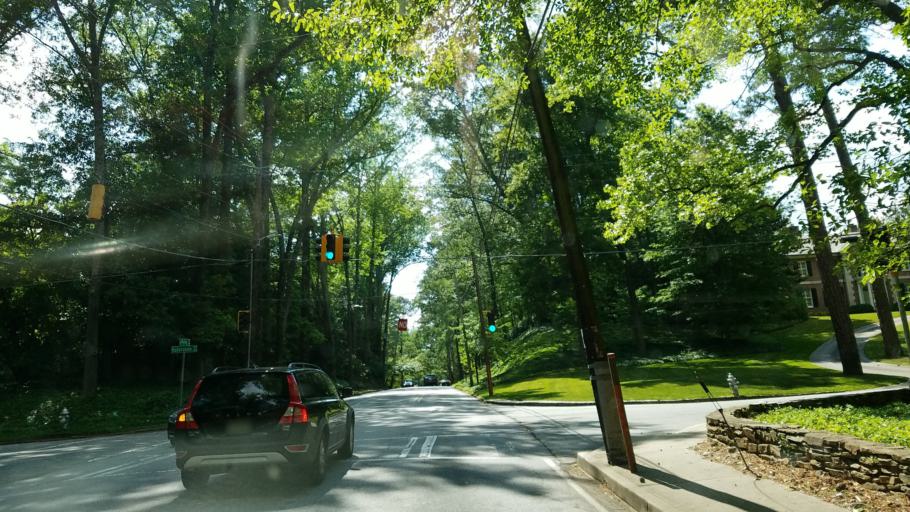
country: US
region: Georgia
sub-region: DeKalb County
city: North Atlanta
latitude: 33.8287
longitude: -84.3941
